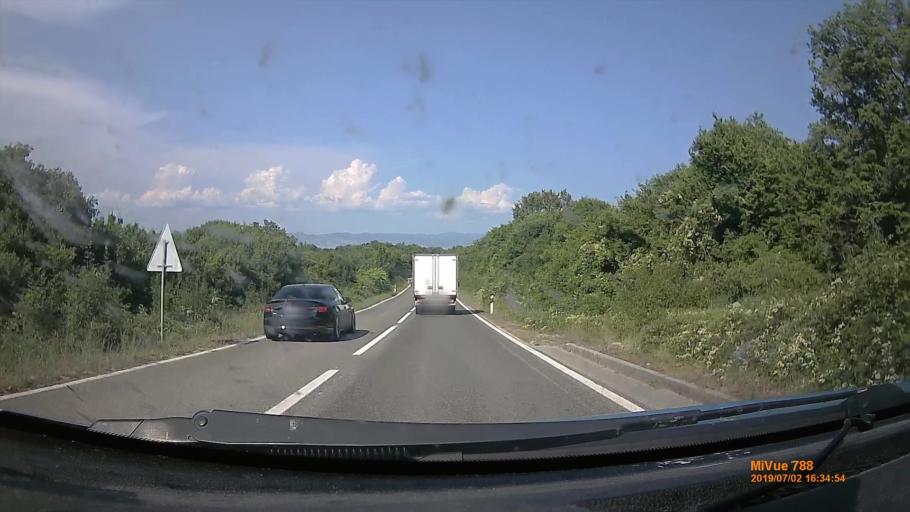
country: HR
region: Primorsko-Goranska
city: Njivice
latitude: 45.0839
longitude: 14.5083
